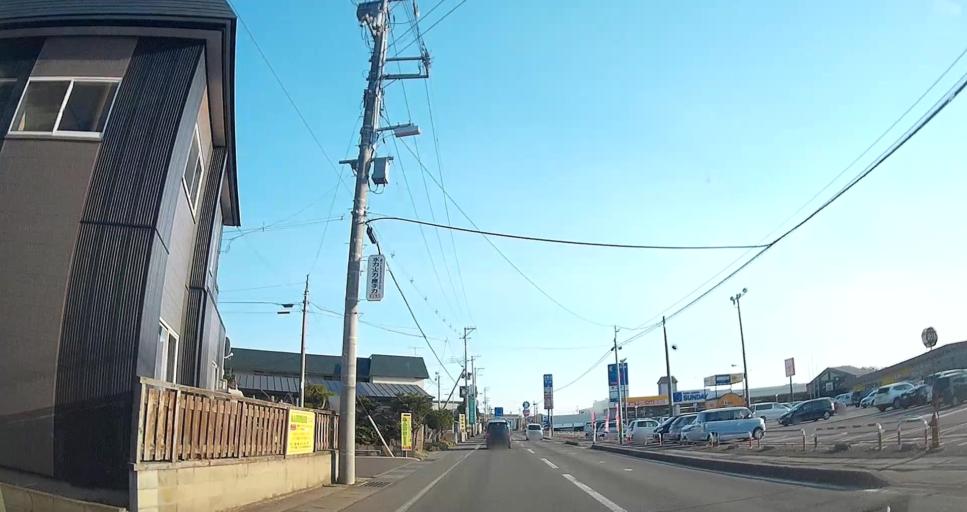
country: JP
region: Aomori
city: Mutsu
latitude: 41.2859
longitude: 141.2114
